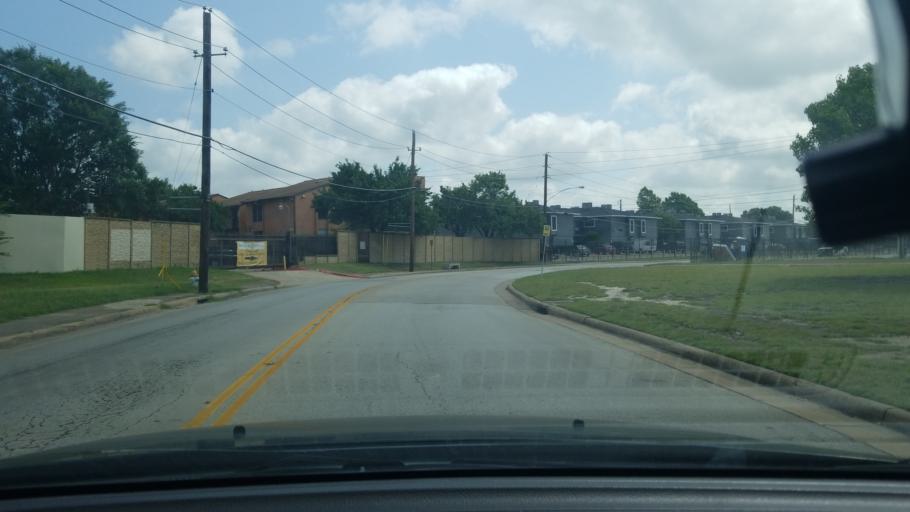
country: US
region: Texas
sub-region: Dallas County
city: Mesquite
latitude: 32.7998
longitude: -96.6904
